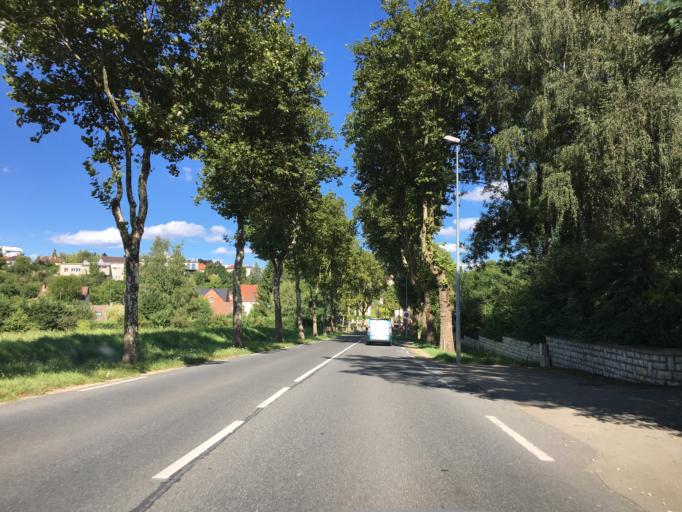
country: FR
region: Bourgogne
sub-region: Departement de l'Yonne
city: Saint-Georges-sur-Baulche
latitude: 47.7890
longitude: 3.5475
